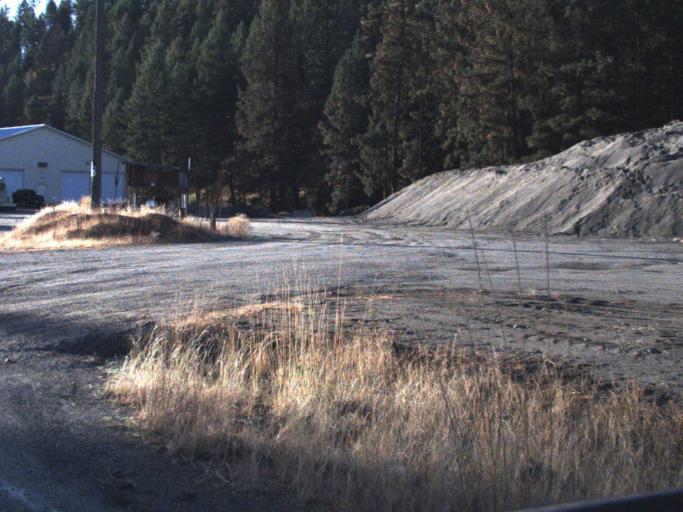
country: US
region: Washington
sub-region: Okanogan County
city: Coulee Dam
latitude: 48.0736
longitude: -118.6784
